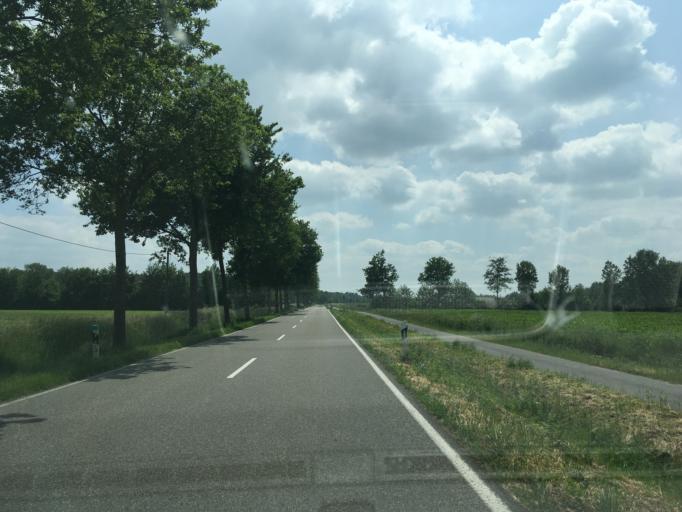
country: DE
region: North Rhine-Westphalia
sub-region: Regierungsbezirk Munster
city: Rhede
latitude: 51.8040
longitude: 6.7548
